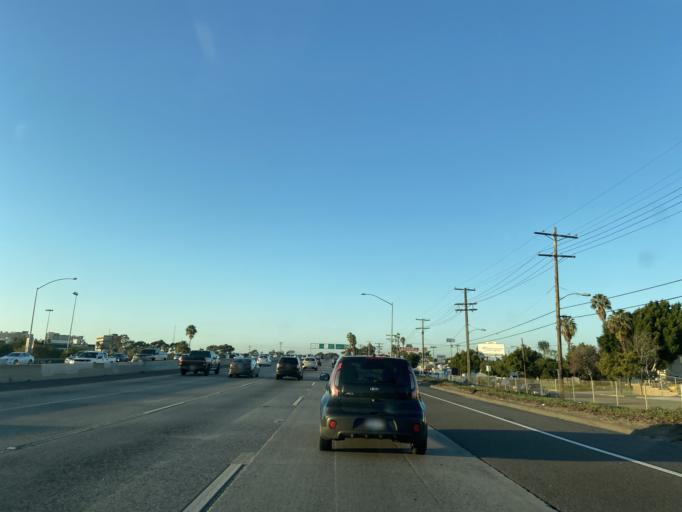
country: US
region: California
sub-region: San Diego County
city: National City
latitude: 32.6791
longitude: -117.1096
